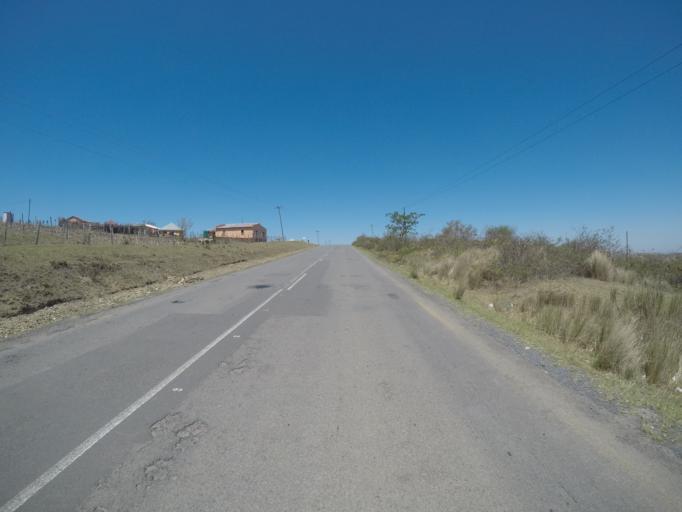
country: ZA
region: Eastern Cape
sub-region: OR Tambo District Municipality
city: Mthatha
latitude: -31.9051
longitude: 28.9479
